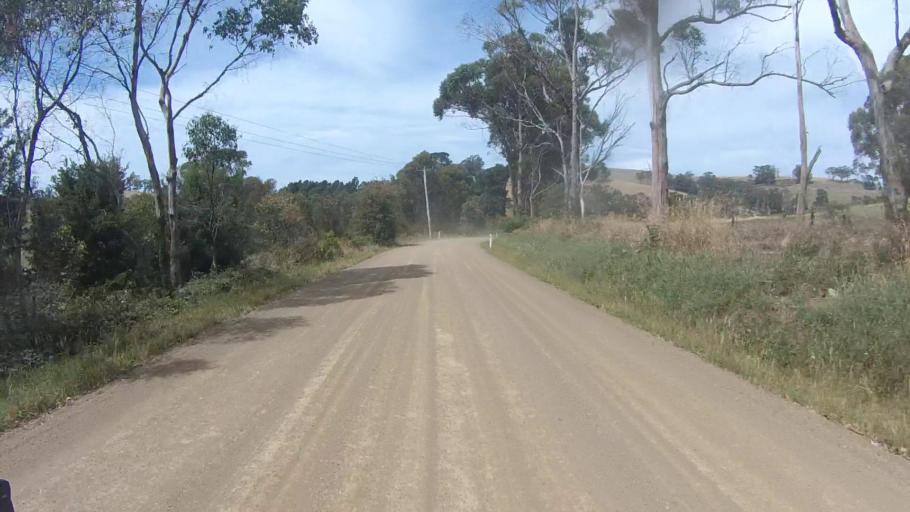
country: AU
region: Tasmania
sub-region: Sorell
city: Sorell
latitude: -42.8188
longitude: 147.8239
